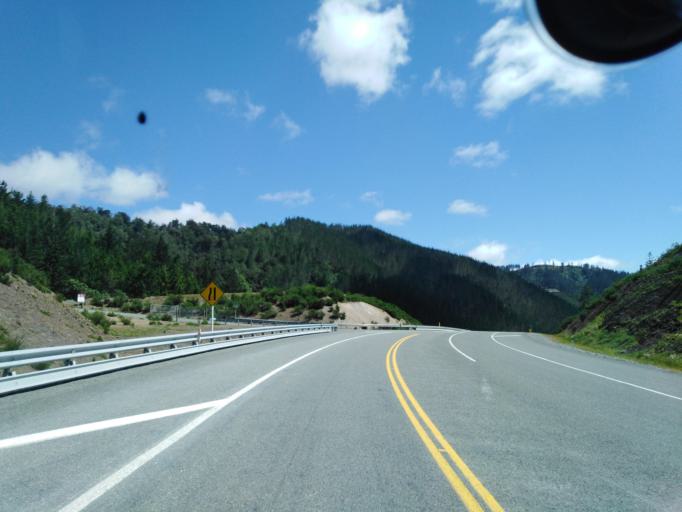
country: NZ
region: Nelson
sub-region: Nelson City
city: Nelson
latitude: -41.1911
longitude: 173.5544
